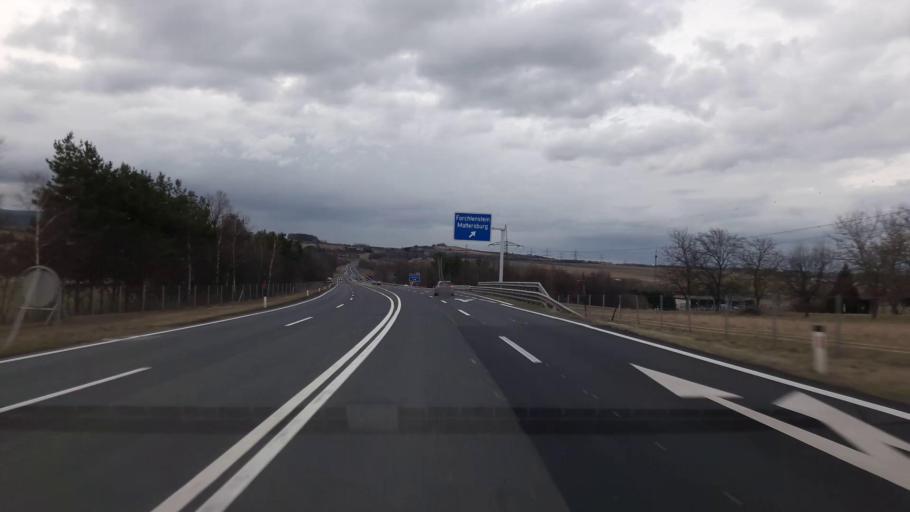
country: AT
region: Burgenland
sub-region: Politischer Bezirk Mattersburg
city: Mattersburg
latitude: 47.7185
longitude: 16.3841
